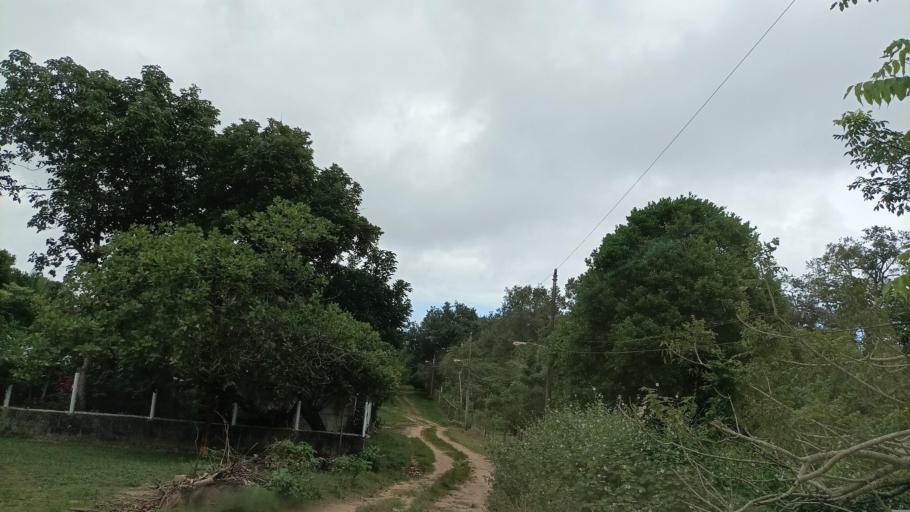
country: MX
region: Veracruz
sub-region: Cosoleacaque
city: Residencial las Olas
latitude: 18.0724
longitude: -94.5851
